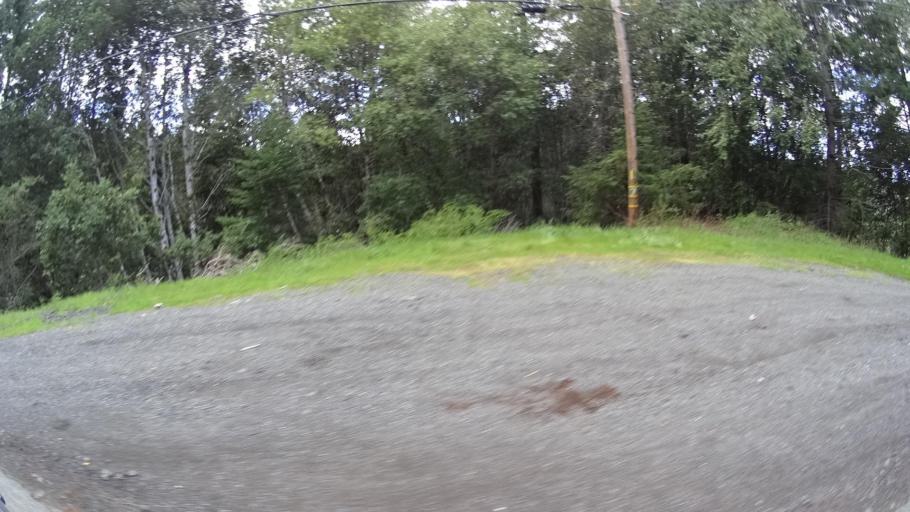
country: US
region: California
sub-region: Humboldt County
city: Bayside
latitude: 40.7526
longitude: -123.9725
